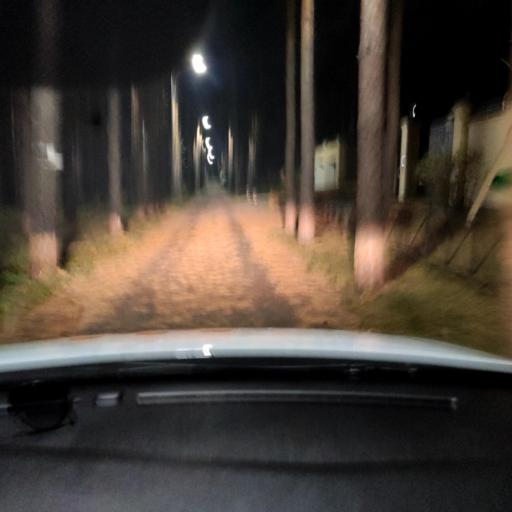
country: RU
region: Tatarstan
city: Verkhniy Uslon
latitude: 55.6216
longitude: 49.0203
